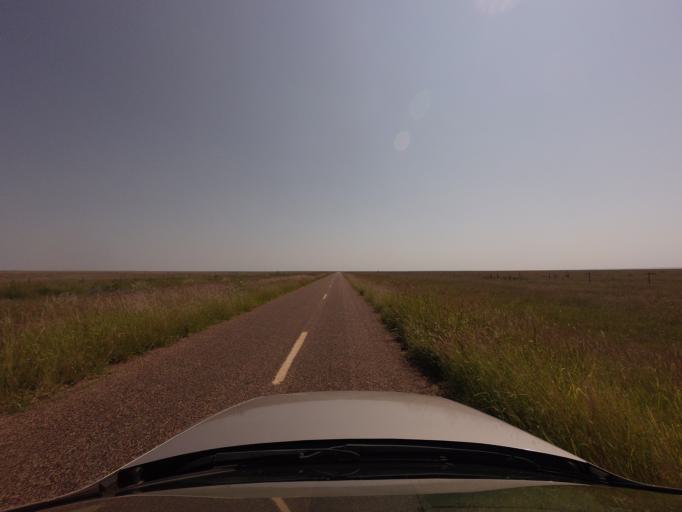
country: US
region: New Mexico
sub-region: Curry County
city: Cannon Air Force Base
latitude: 34.6333
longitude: -103.4335
